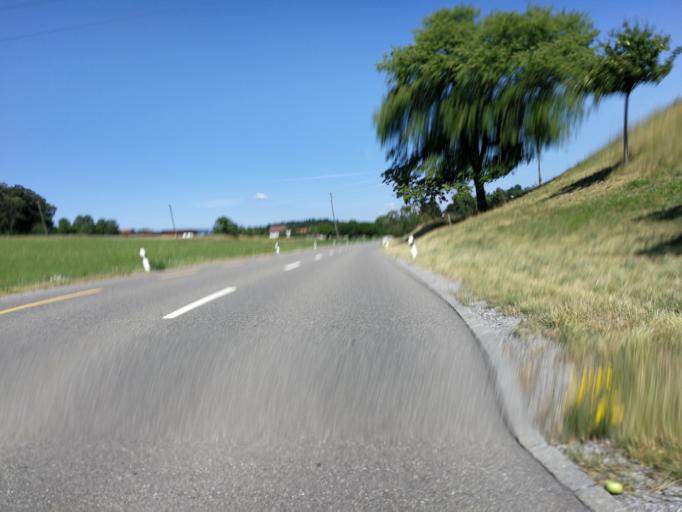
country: CH
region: Zurich
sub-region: Bezirk Hinwil
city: Gossau
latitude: 47.3240
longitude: 8.7509
